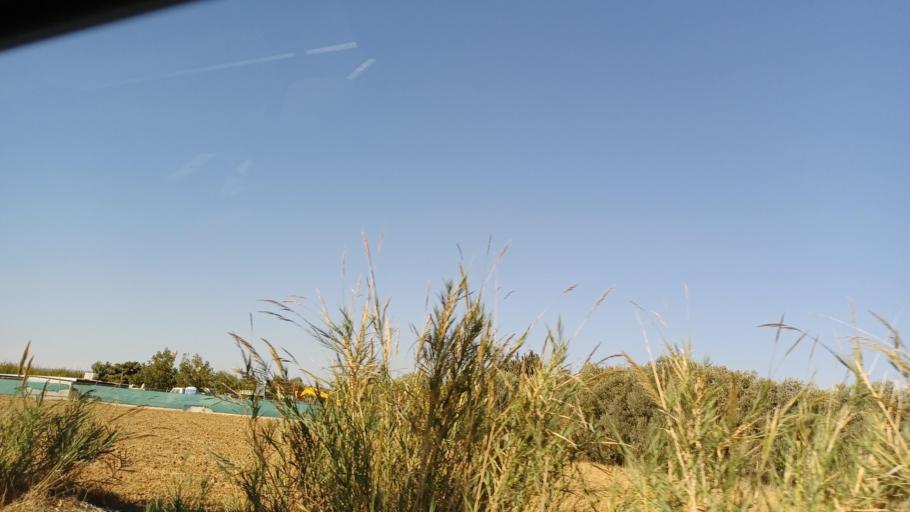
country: CY
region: Larnaka
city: Kolossi
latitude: 34.6656
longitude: 32.9457
